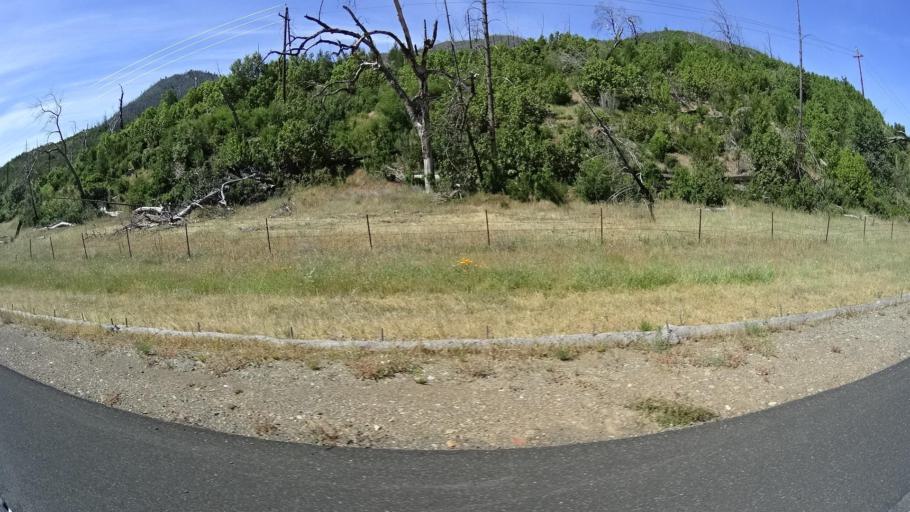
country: US
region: California
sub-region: Lake County
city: Middletown
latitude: 38.7709
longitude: -122.6610
